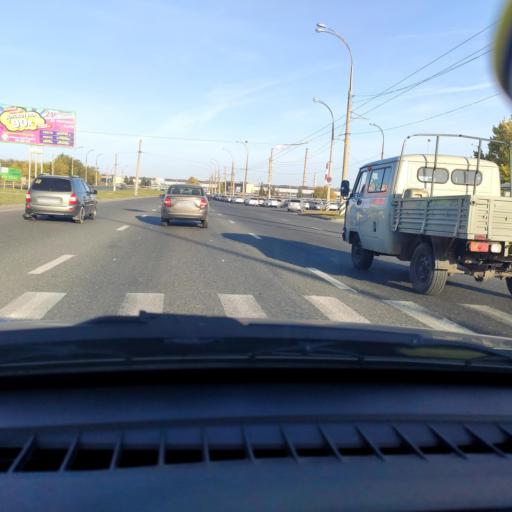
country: RU
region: Samara
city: Tol'yatti
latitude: 53.5532
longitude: 49.2615
